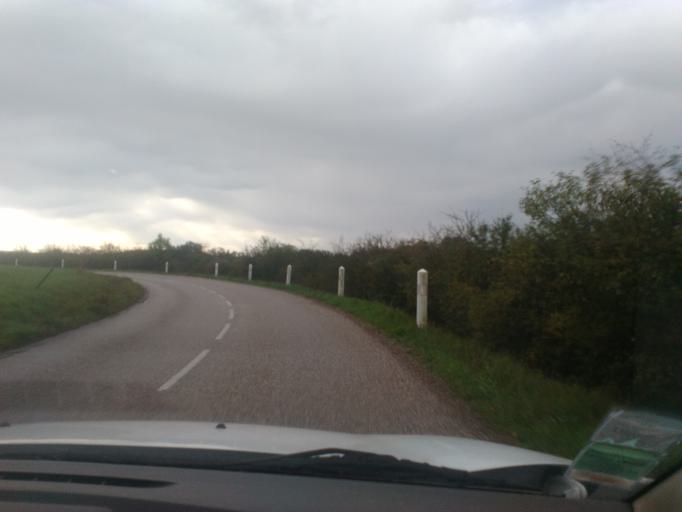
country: FR
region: Lorraine
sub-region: Departement des Vosges
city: Dogneville
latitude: 48.2642
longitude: 6.5017
